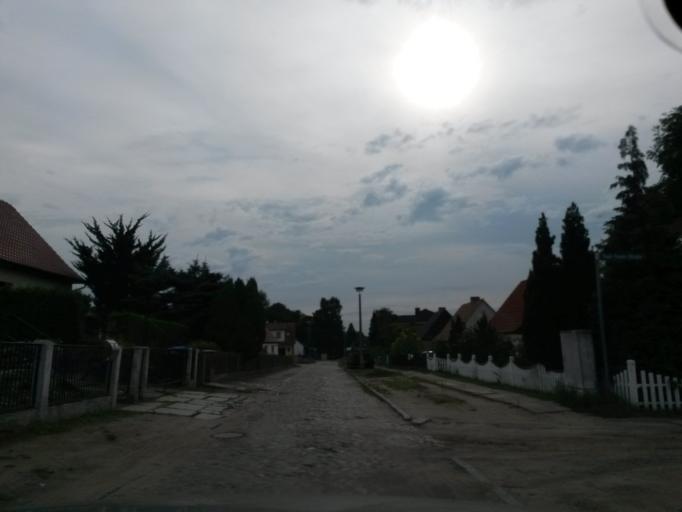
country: DE
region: Brandenburg
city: Eberswalde
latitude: 52.8339
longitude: 13.8452
